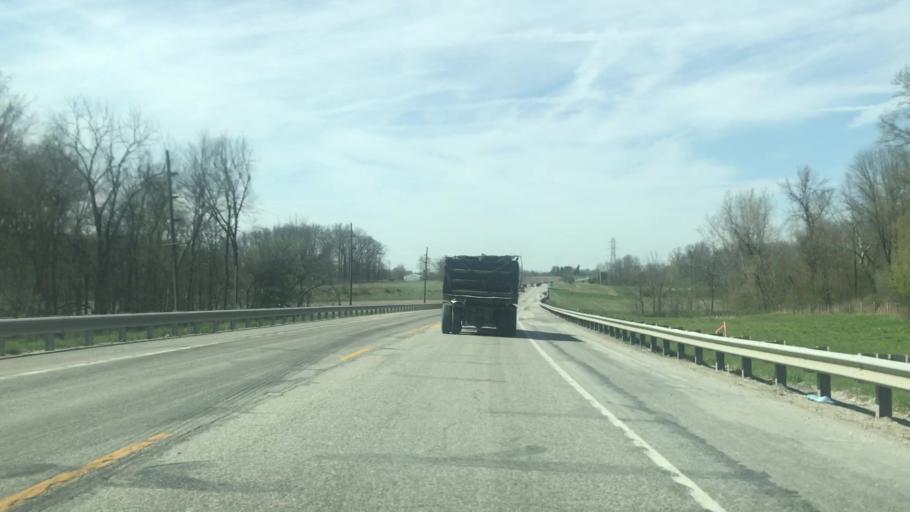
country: US
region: Indiana
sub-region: Putnam County
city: Cloverdale
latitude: 39.5521
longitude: -86.8103
